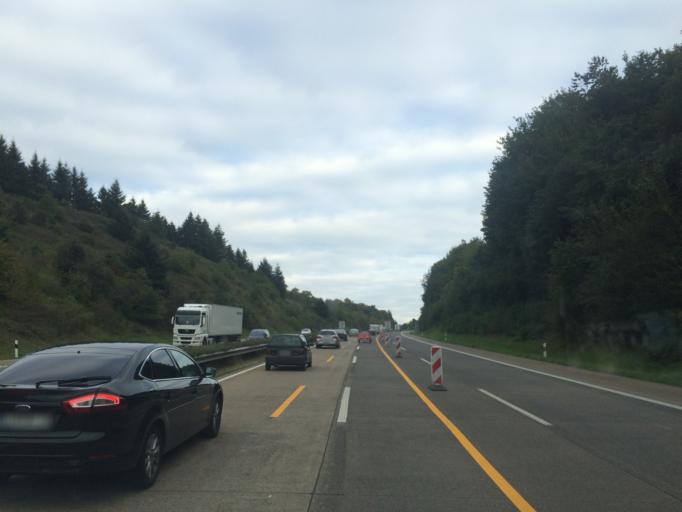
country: DE
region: Rheinland-Pfalz
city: Mehring
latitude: 49.7836
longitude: 6.8272
